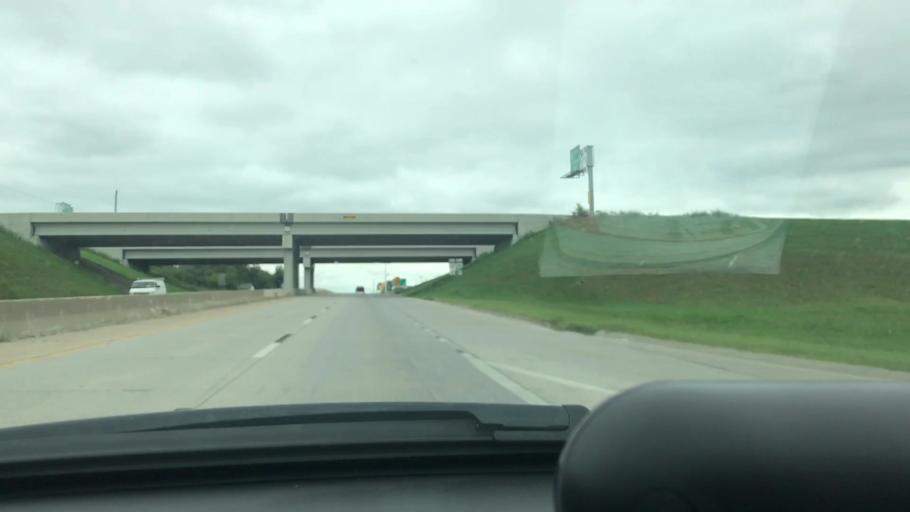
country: US
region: Oklahoma
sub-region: Mayes County
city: Chouteau
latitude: 36.1654
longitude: -95.3418
